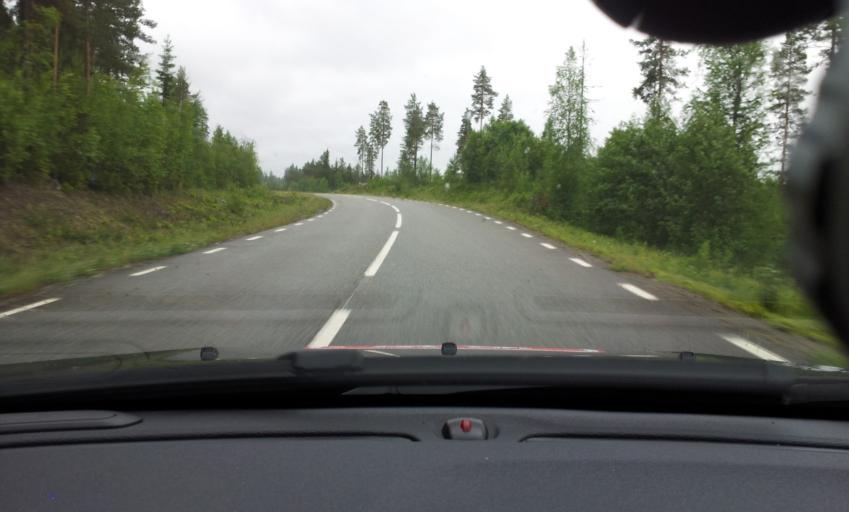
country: SE
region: Jaemtland
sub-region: Stroemsunds Kommun
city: Stroemsund
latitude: 63.3815
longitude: 15.6852
